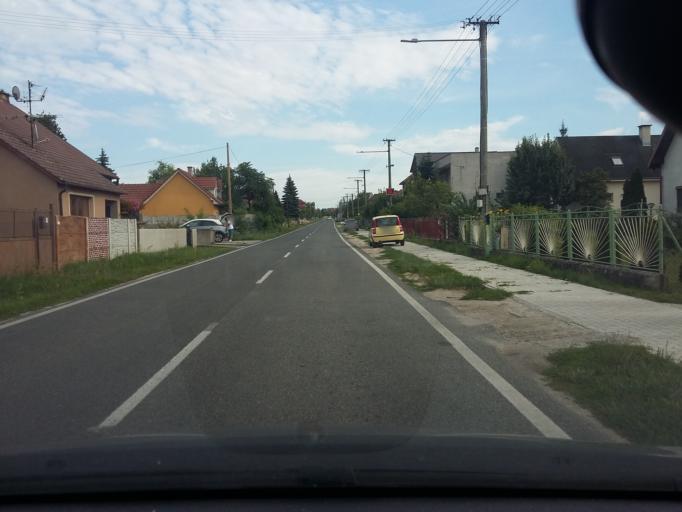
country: SK
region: Trnavsky
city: Gbely
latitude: 48.6375
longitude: 17.1999
